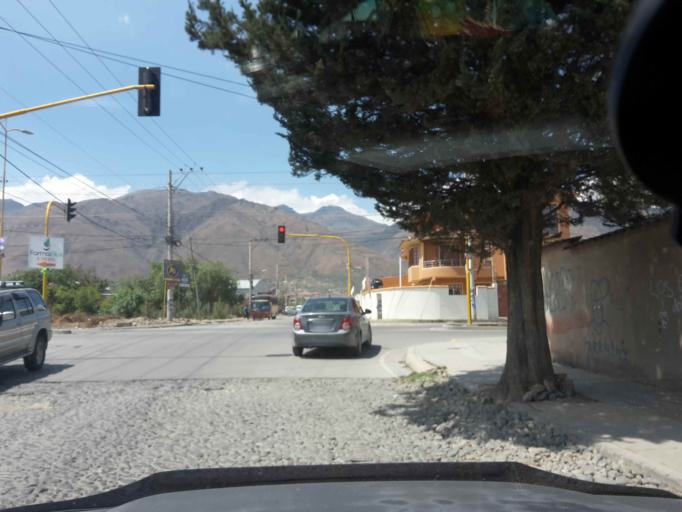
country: BO
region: Cochabamba
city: Cochabamba
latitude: -17.3439
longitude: -66.2019
